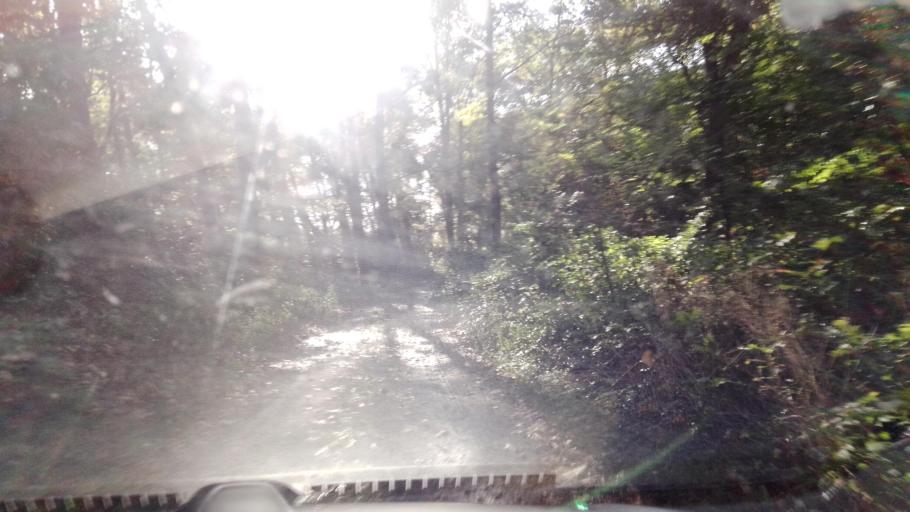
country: NL
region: Limburg
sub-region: Gemeente Venlo
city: Arcen
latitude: 51.4354
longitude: 6.1739
